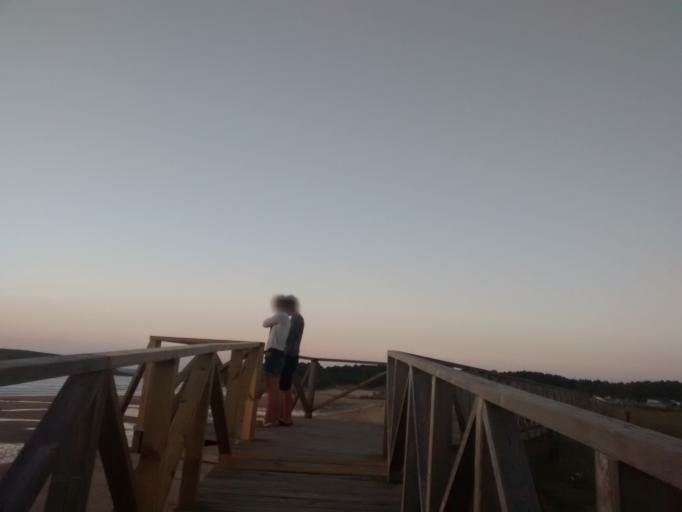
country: ES
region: Cantabria
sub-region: Provincia de Cantabria
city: Santander
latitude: 43.4608
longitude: -3.7286
